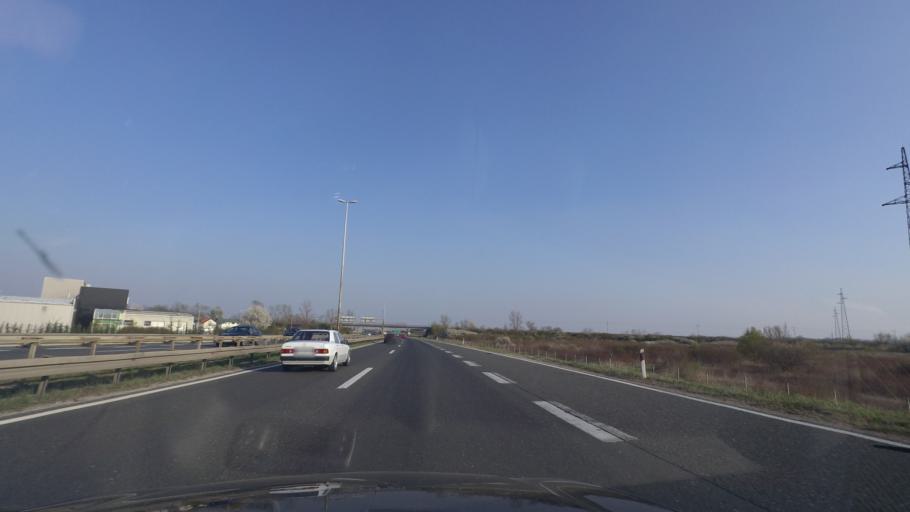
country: HR
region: Grad Zagreb
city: Zadvorsko
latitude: 45.7533
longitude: 15.9066
